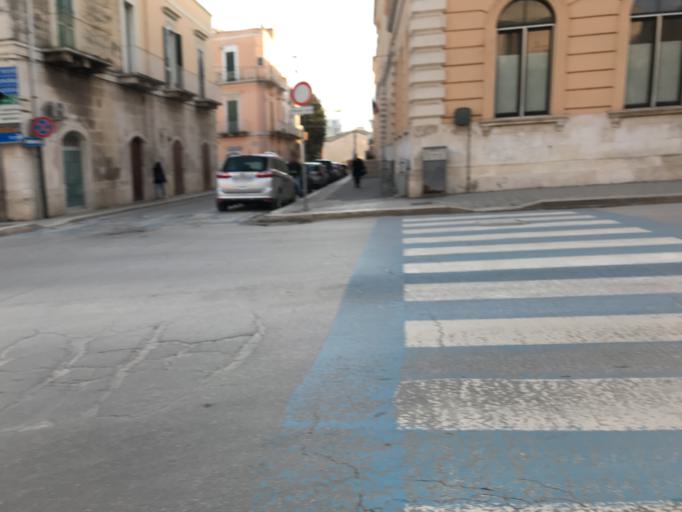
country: IT
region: Apulia
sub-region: Provincia di Bari
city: Corato
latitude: 41.1490
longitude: 16.4116
